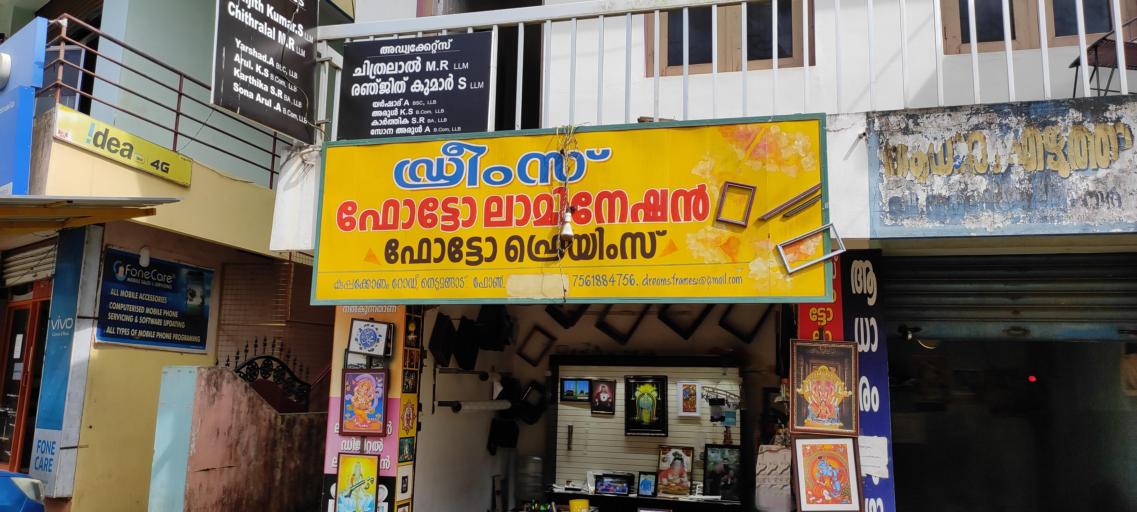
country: IN
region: Kerala
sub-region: Thiruvananthapuram
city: Nedumangad
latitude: 8.6070
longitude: 77.0020
